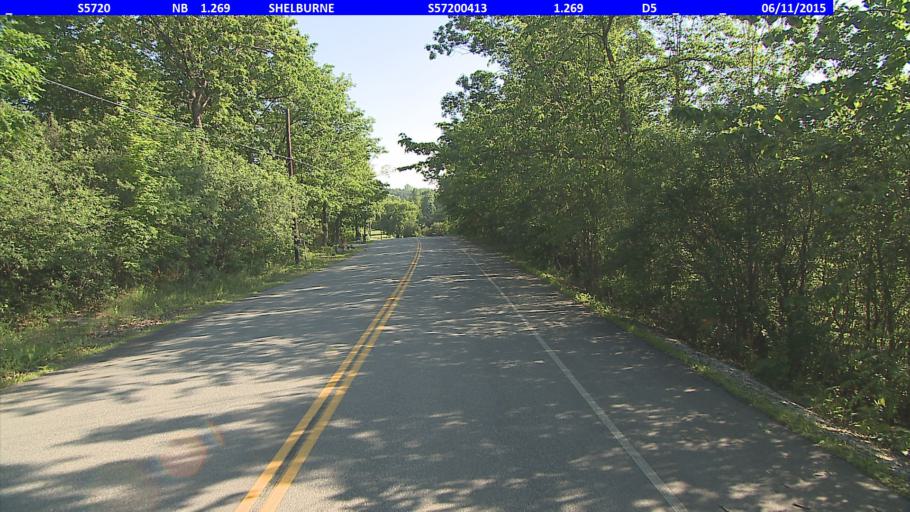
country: US
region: Vermont
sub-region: Chittenden County
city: South Burlington
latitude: 44.3862
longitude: -73.2011
